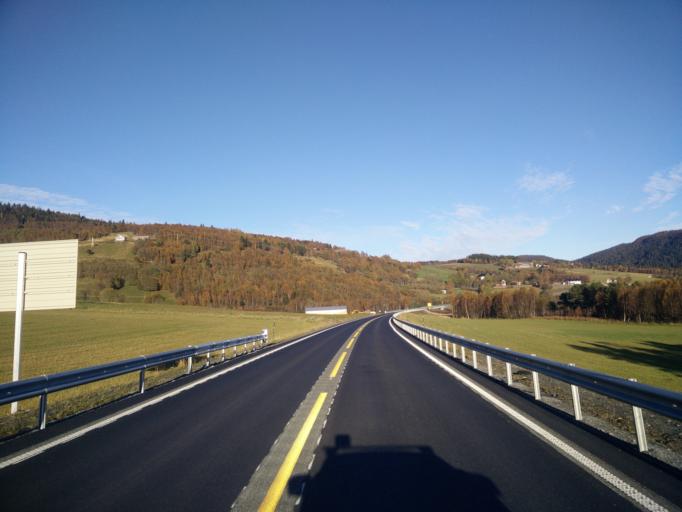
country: NO
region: Sor-Trondelag
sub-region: Snillfjord
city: Krokstadora
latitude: 63.2835
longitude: 9.6130
